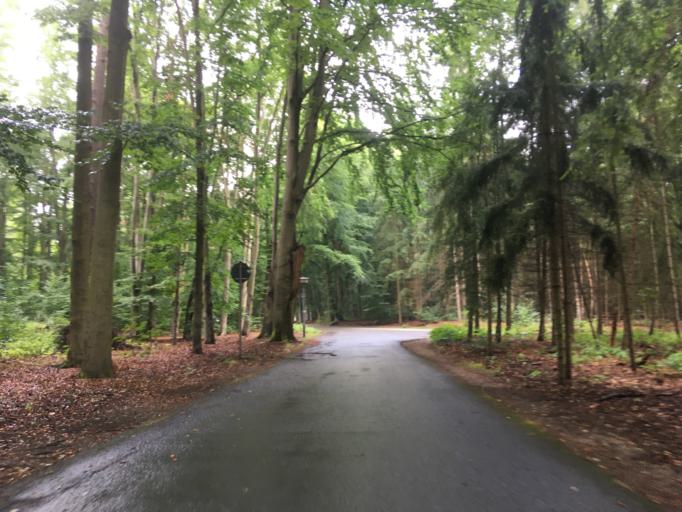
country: DE
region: Brandenburg
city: Joachimsthal
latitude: 52.9236
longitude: 13.7299
